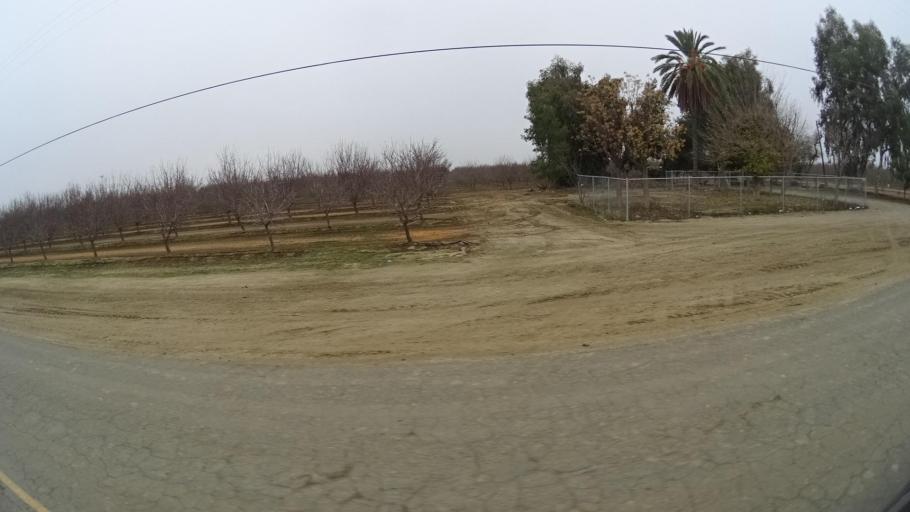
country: US
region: California
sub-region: Kern County
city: Lost Hills
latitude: 35.5982
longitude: -119.5269
